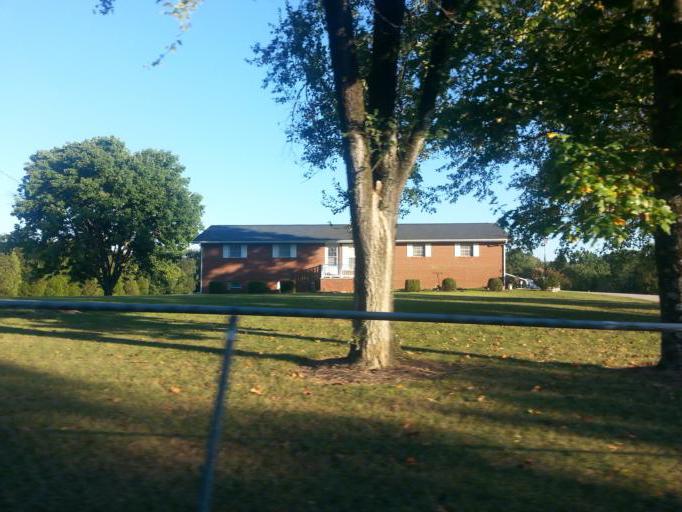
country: US
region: Tennessee
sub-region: Blount County
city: Wildwood
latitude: 35.8362
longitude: -83.8811
